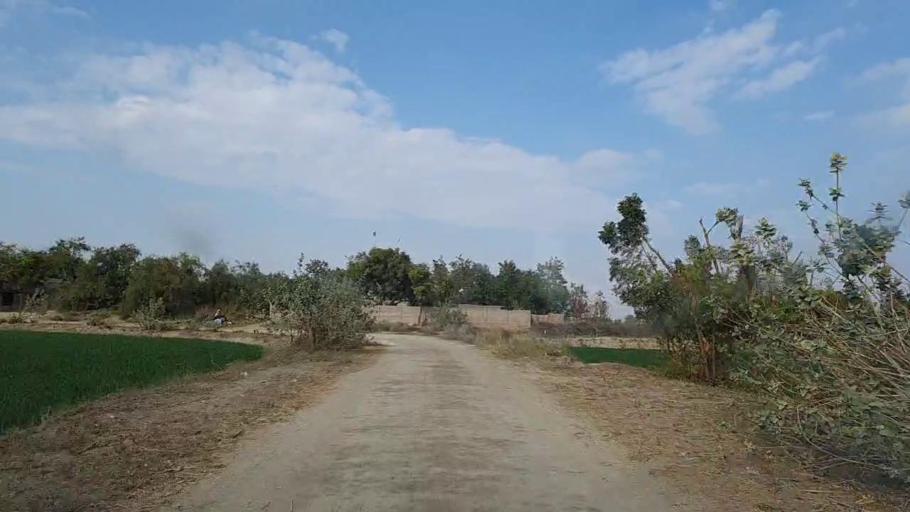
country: PK
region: Sindh
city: Sanghar
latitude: 26.2456
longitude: 69.0167
